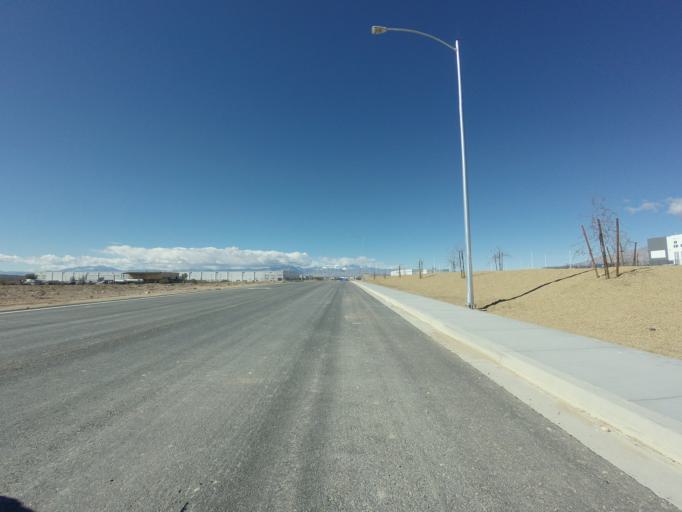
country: US
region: Nevada
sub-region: Clark County
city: Nellis Air Force Base
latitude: 36.2623
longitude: -115.0403
